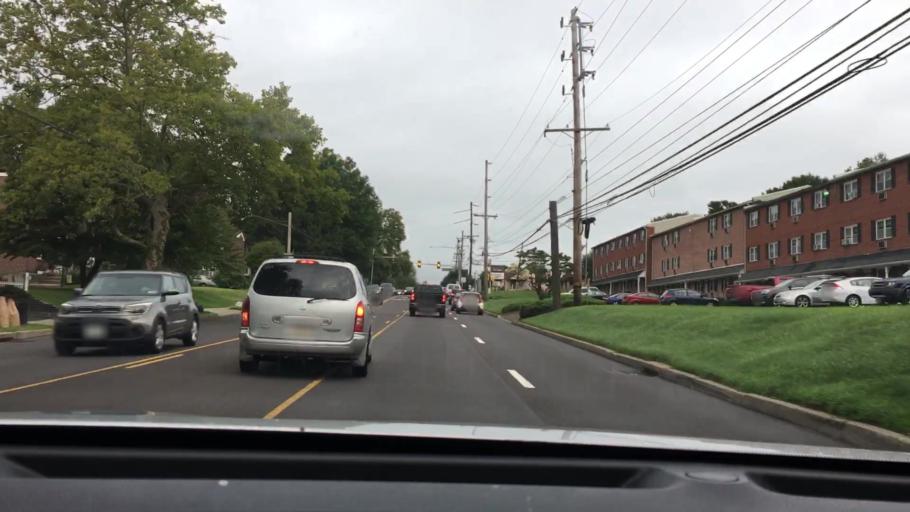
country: US
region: Pennsylvania
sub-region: Montgomery County
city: Hatboro
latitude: 40.1879
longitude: -75.0994
